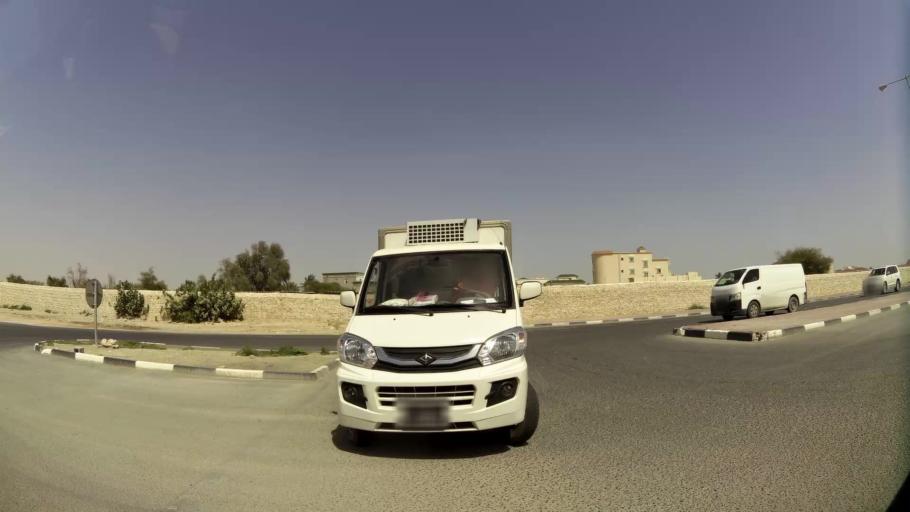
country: QA
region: Baladiyat Umm Salal
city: Umm Salal Muhammad
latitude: 25.3935
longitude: 51.4191
